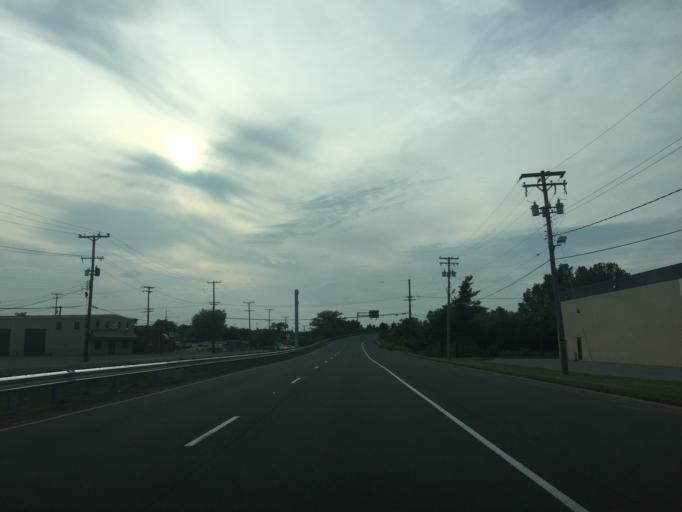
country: US
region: Maryland
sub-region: Baltimore County
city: Essex
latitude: 39.2818
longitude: -76.4875
